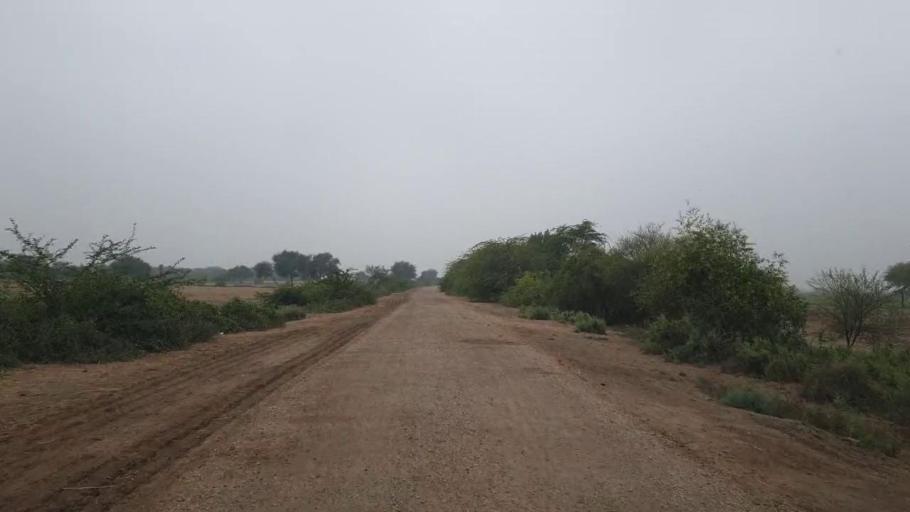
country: PK
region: Sindh
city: Badin
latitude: 24.6029
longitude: 68.6727
